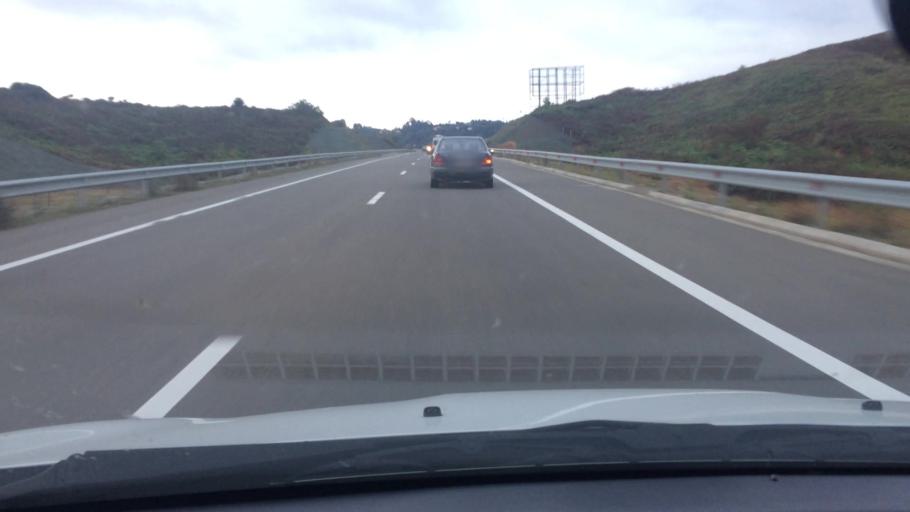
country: GE
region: Ajaria
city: Makhinjauri
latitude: 41.7274
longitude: 41.7507
